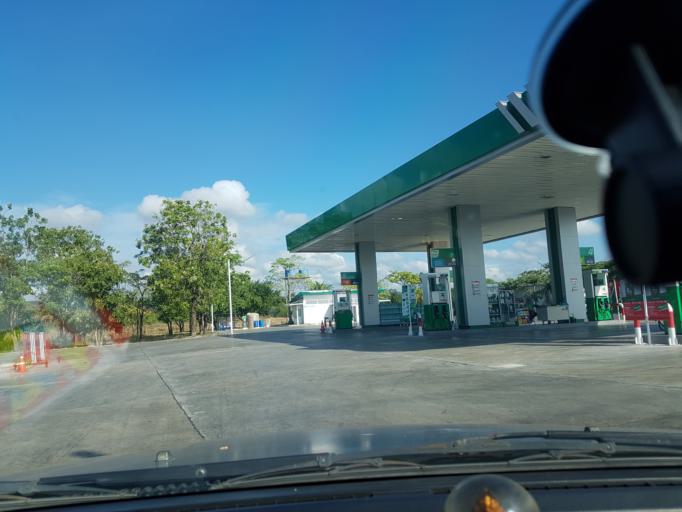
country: TH
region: Lop Buri
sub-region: Amphoe Tha Luang
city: Tha Luang
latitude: 15.0746
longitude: 100.9914
